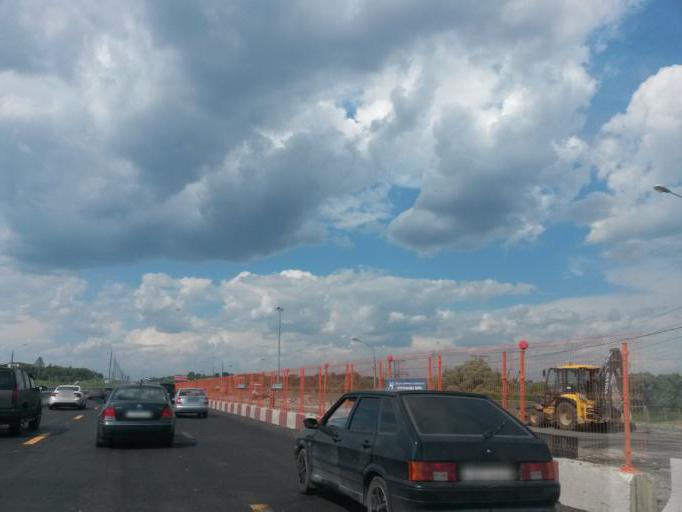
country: RU
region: Moskovskaya
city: Shcherbinka
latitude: 55.4643
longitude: 37.6190
